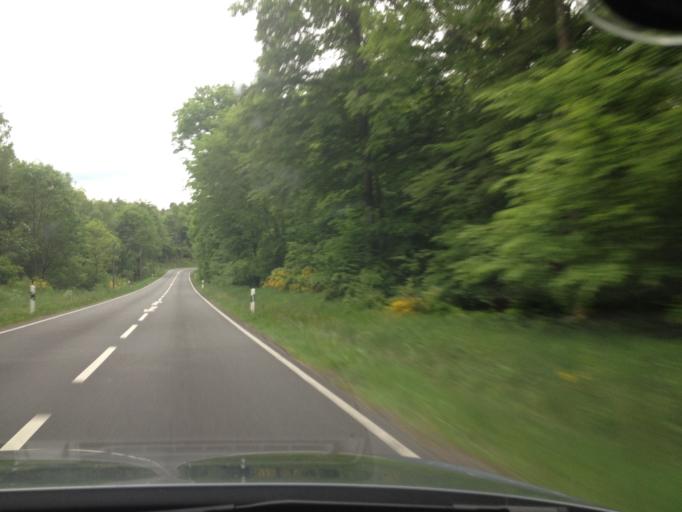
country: DE
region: Saarland
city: Neunkirchen
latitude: 49.3234
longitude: 7.1868
